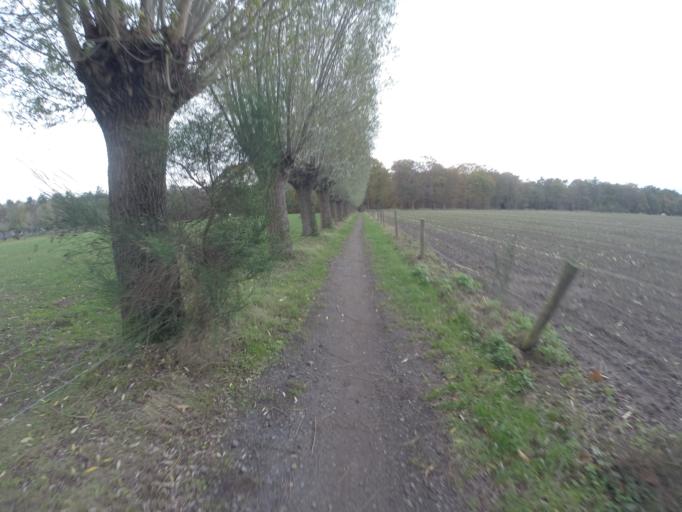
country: BE
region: Flanders
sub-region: Provincie Oost-Vlaanderen
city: Maldegem
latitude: 51.1648
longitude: 3.4493
